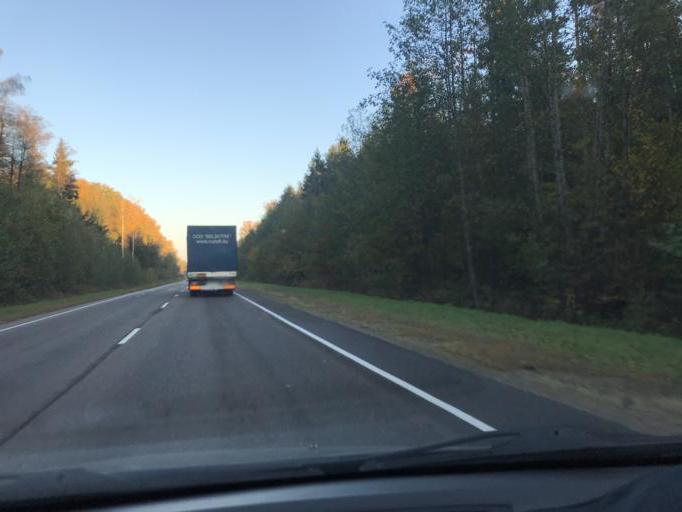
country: BY
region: Minsk
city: Staryya Darohi
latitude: 53.0373
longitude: 28.2069
